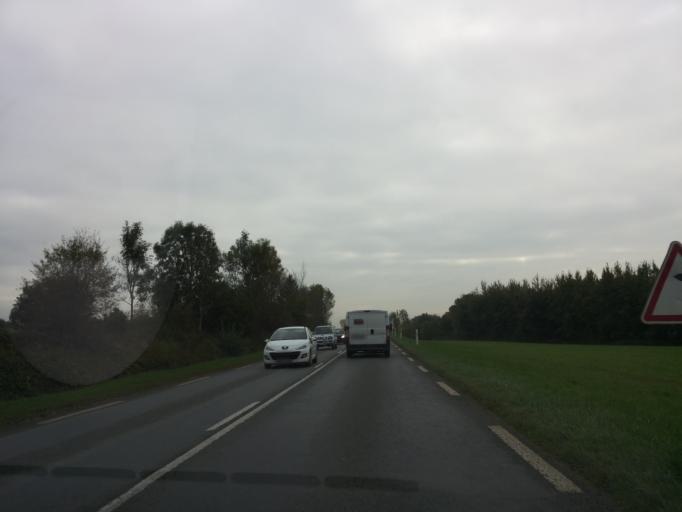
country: FR
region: Champagne-Ardenne
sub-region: Departement des Ardennes
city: Douzy
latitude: 49.6729
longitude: 5.0230
